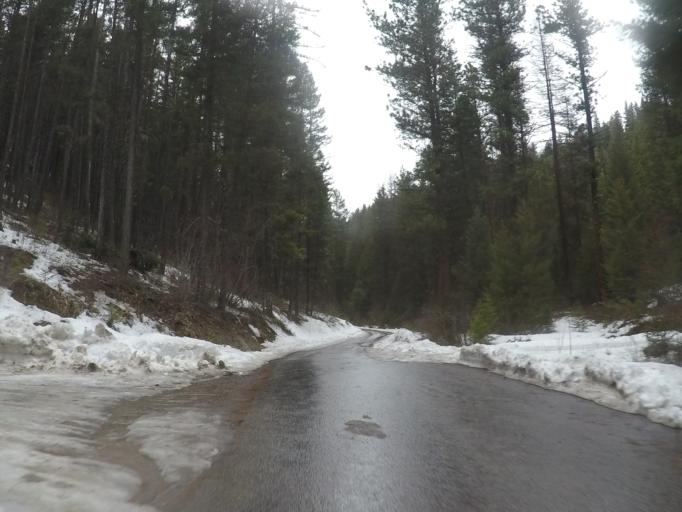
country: US
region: Montana
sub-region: Missoula County
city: East Missoula
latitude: 46.9285
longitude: -113.9672
